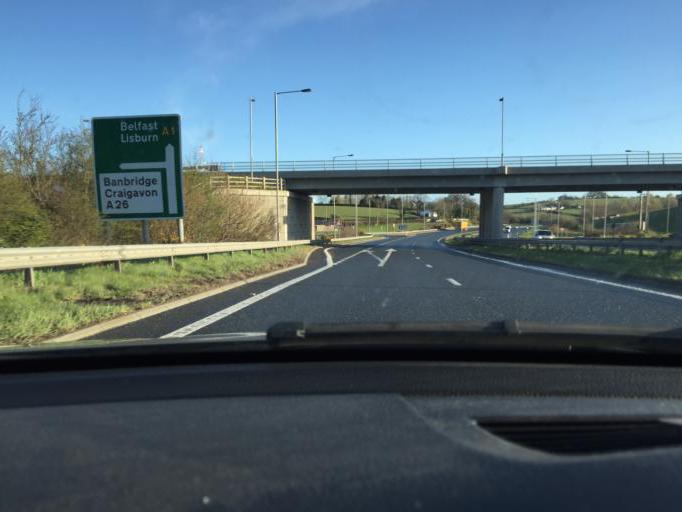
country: GB
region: Northern Ireland
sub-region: Banbridge District
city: Banbridge
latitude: 54.3538
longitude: -6.2403
